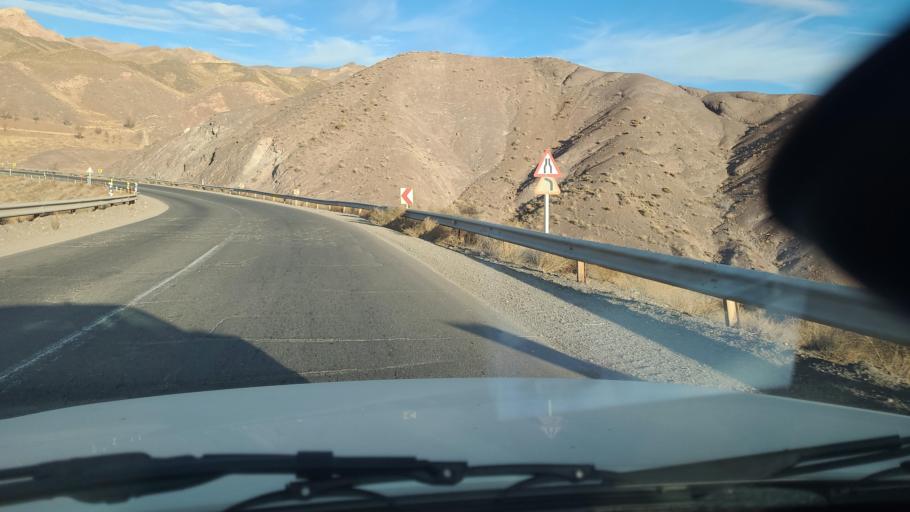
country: IR
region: Razavi Khorasan
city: Sabzevar
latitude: 36.4185
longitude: 57.5644
